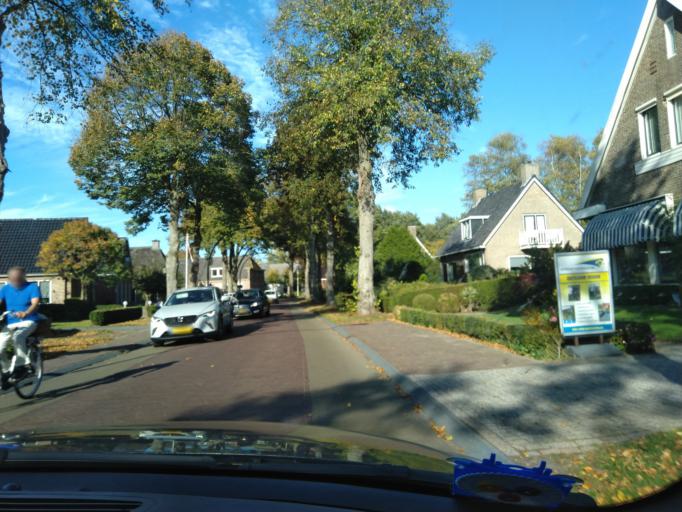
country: NL
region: Drenthe
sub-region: Gemeente Aa en Hunze
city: Anloo
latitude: 53.0343
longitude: 6.6618
